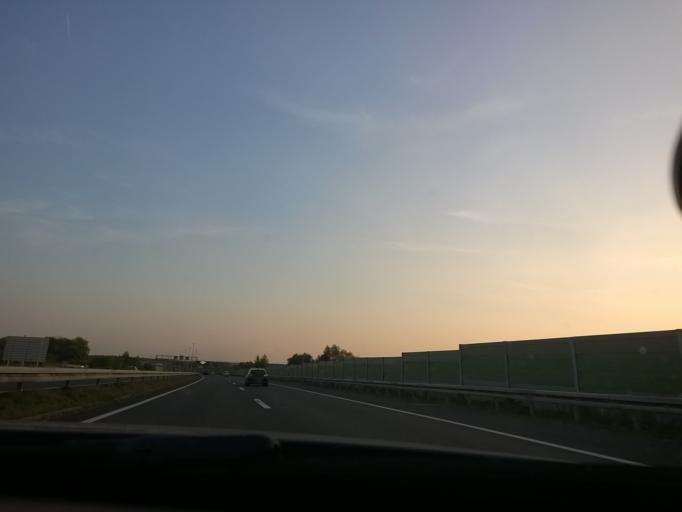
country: HR
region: Grad Zagreb
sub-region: Sesvete
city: Sesvete
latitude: 45.8305
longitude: 16.1370
